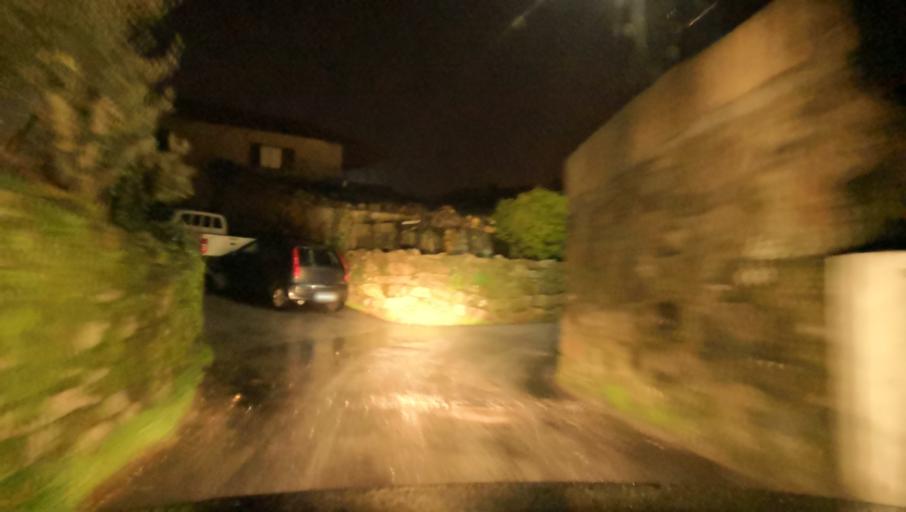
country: PT
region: Vila Real
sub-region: Vila Real
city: Vila Real
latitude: 41.3338
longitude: -7.7238
